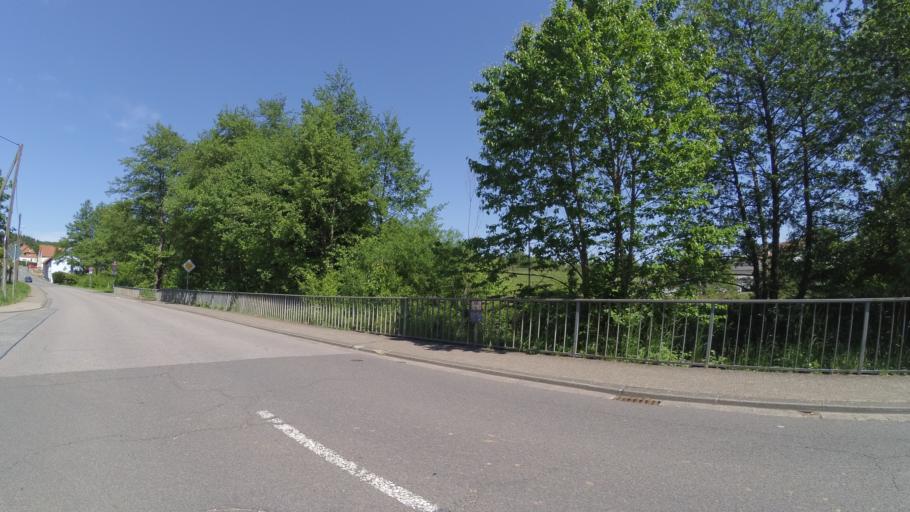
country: DE
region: Saarland
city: Heusweiler
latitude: 49.3613
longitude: 6.9366
